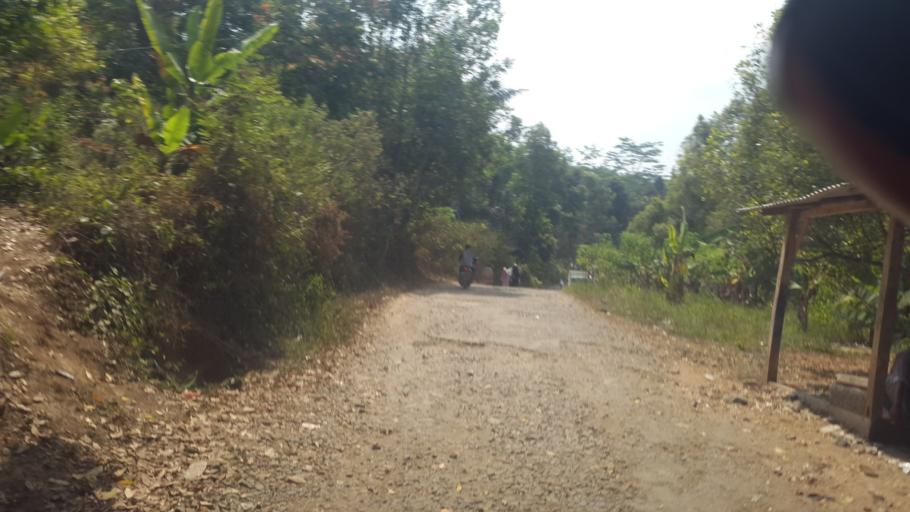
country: ID
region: West Java
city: Nagrak
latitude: -6.8995
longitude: 106.5241
